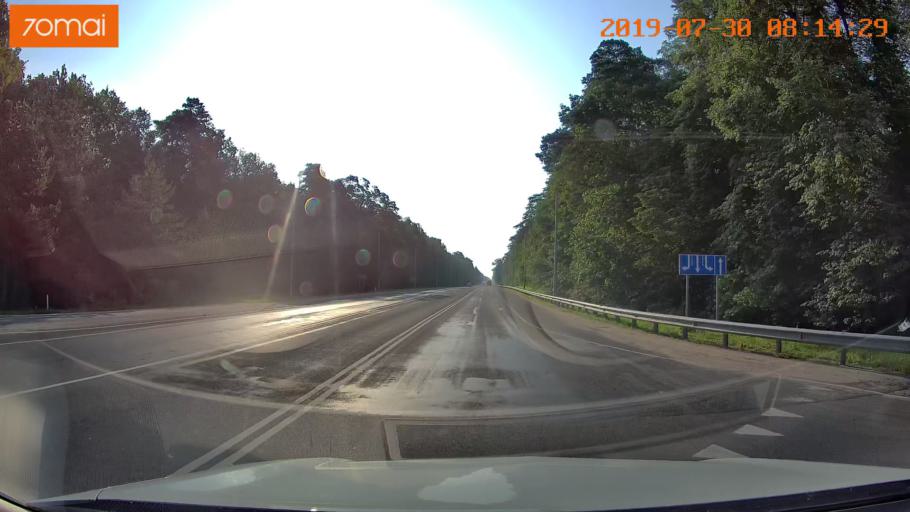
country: RU
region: Kaliningrad
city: Zheleznodorozhnyy
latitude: 54.6479
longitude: 21.3600
